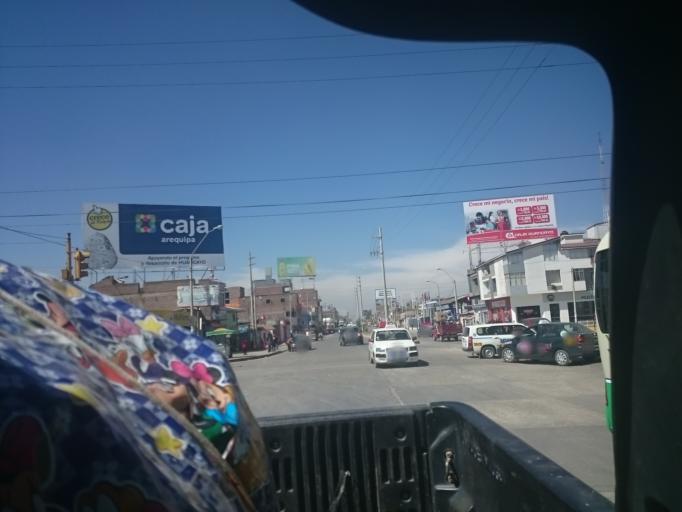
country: PE
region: Junin
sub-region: Provincia de Huancayo
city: Pilcomay
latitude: -12.0433
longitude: -75.2261
